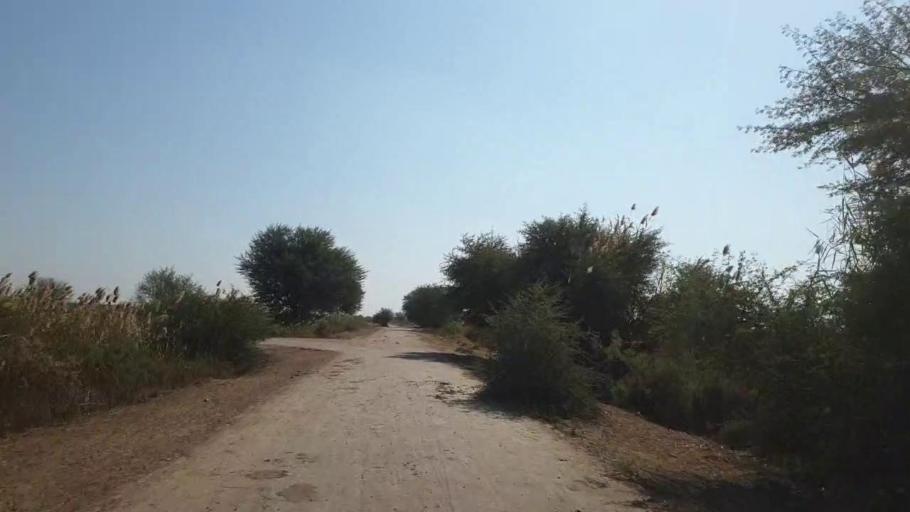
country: PK
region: Sindh
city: Mirpur Khas
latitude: 25.6350
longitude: 69.0282
